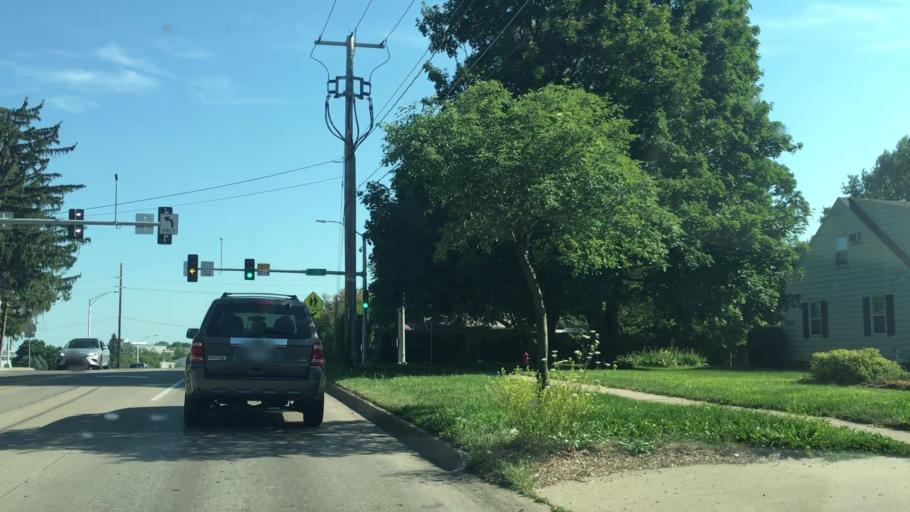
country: US
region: Iowa
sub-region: Johnson County
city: Iowa City
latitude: 41.6467
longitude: -91.5021
